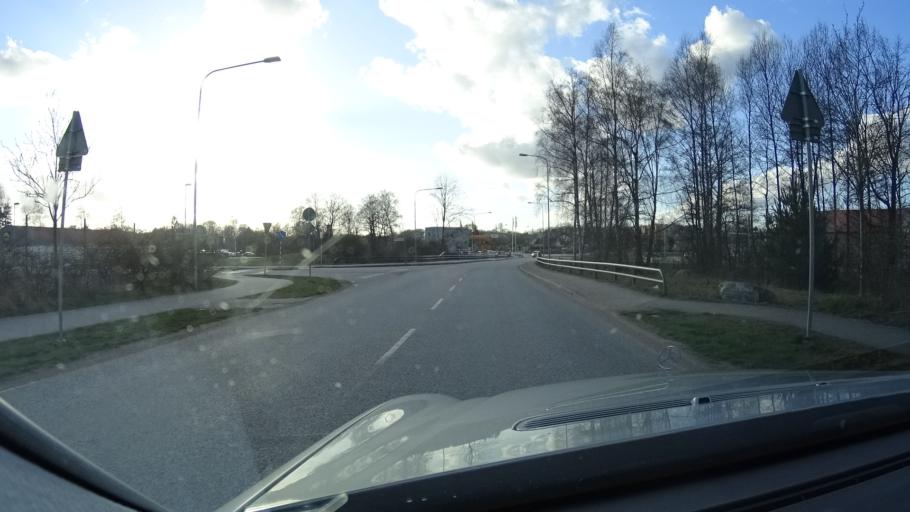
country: SE
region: Skane
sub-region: Hoors Kommun
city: Satofta
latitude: 55.9254
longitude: 13.5481
